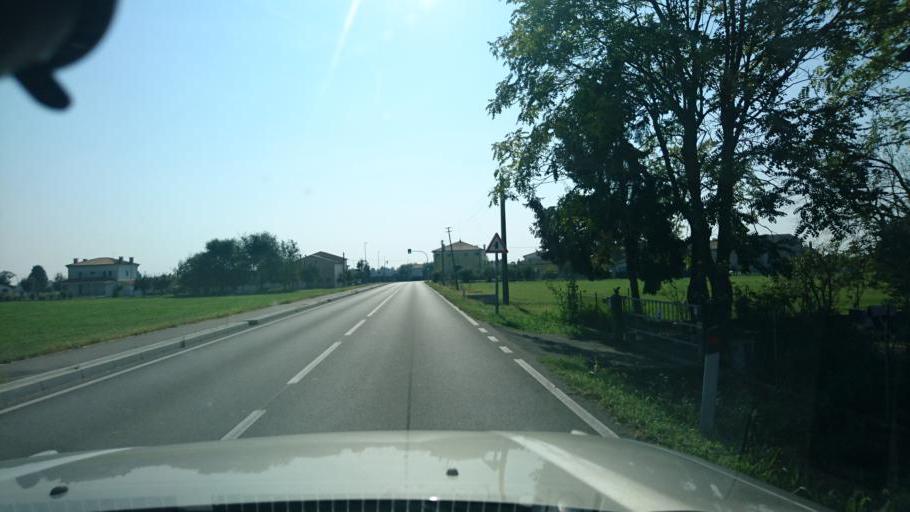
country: IT
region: Veneto
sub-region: Provincia di Padova
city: Gazzo
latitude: 45.5709
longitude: 11.7105
